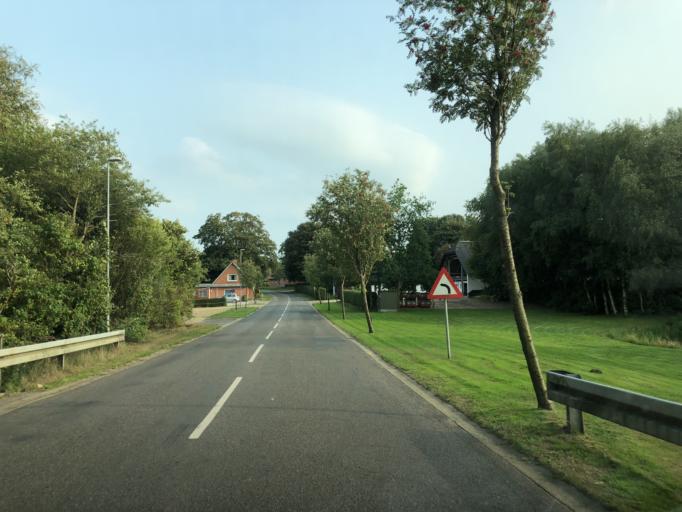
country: DK
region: Central Jutland
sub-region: Ringkobing-Skjern Kommune
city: Videbaek
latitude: 56.0562
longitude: 8.6883
